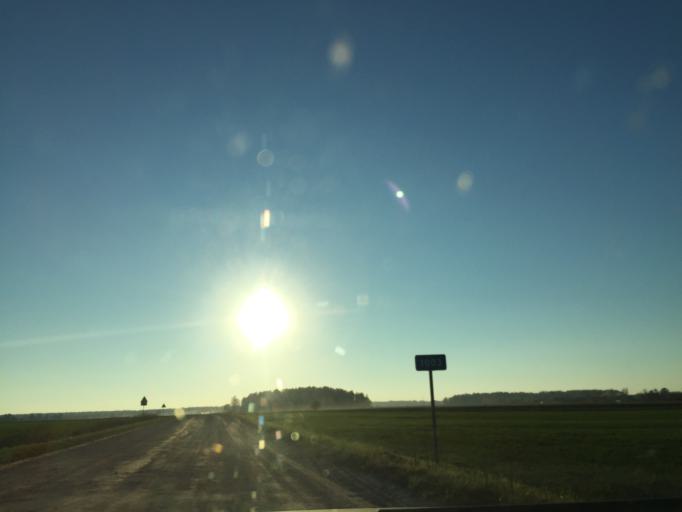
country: LT
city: Vieksniai
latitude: 56.3118
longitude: 22.5521
